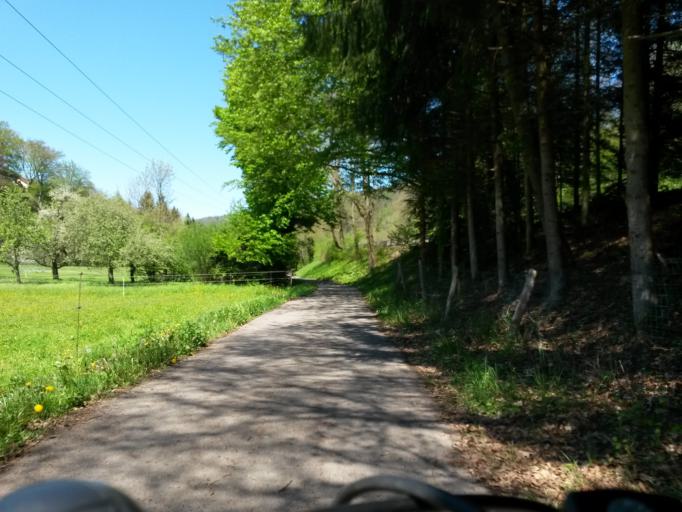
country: DE
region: Baden-Wuerttemberg
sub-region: Karlsruhe Region
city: Unterreichenbach
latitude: 48.8172
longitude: 8.7154
